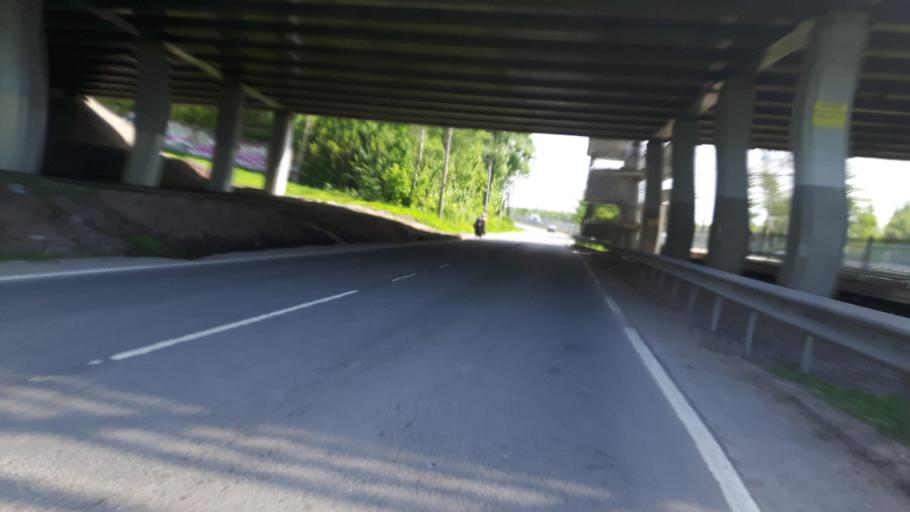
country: RU
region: Leningrad
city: Gorskaya
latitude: 60.0392
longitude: 29.9775
